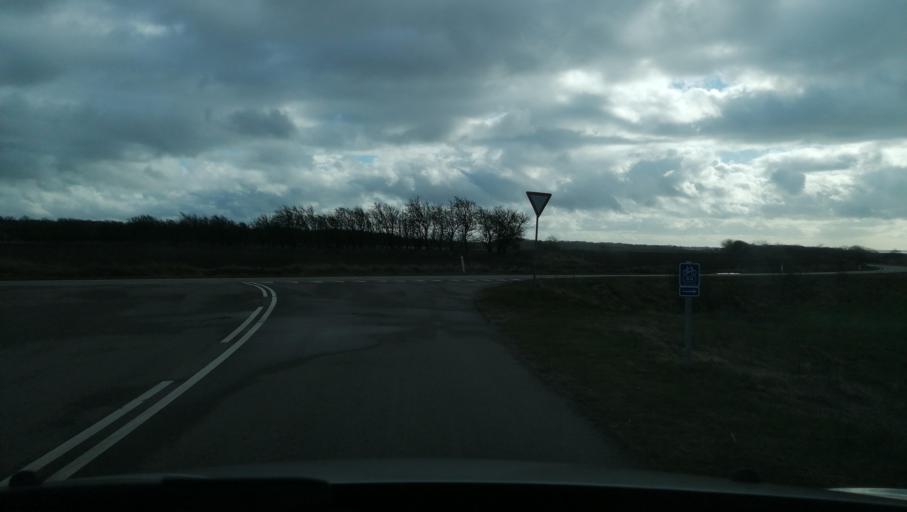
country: DK
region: Zealand
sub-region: Odsherred Kommune
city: Horve
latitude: 55.7807
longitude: 11.3956
